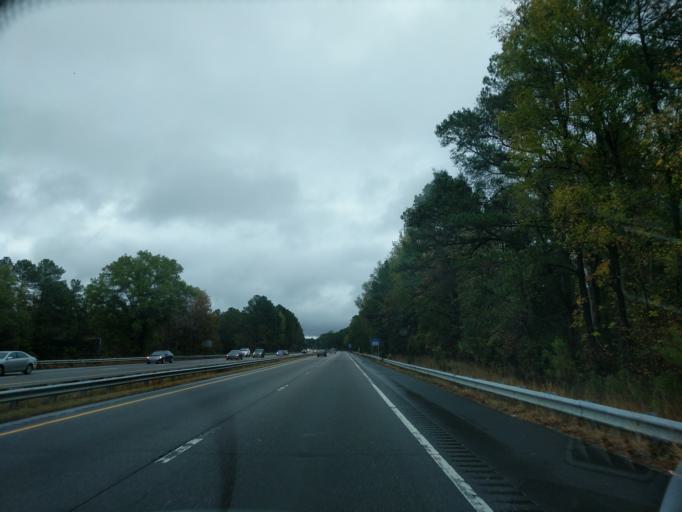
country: US
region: North Carolina
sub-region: Durham County
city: Gorman
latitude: 36.0364
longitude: -78.8320
